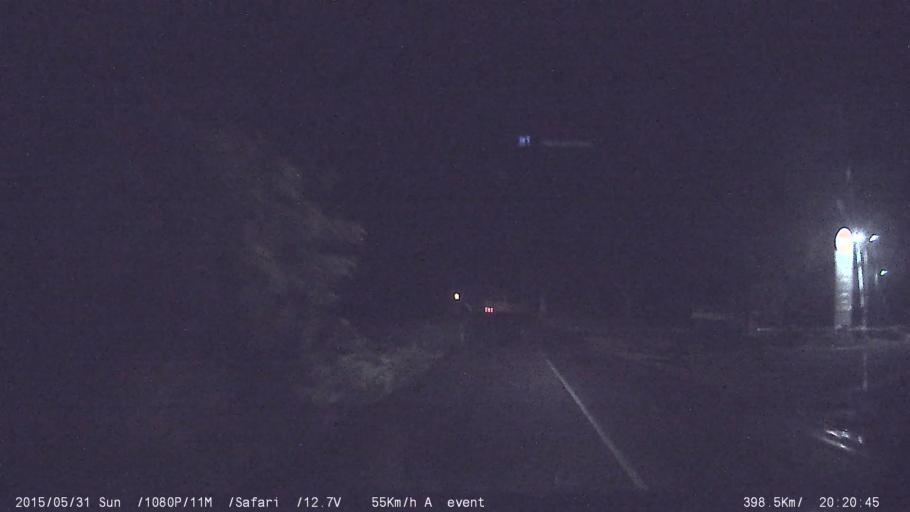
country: IN
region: Karnataka
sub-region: Mandya
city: Malavalli
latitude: 12.4206
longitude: 77.2083
